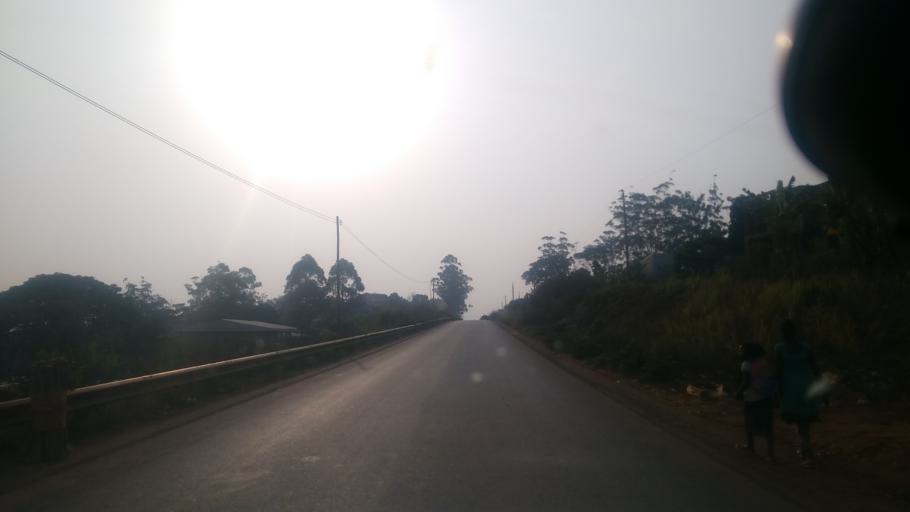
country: CM
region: West
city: Bangangte
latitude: 5.1554
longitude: 10.4562
